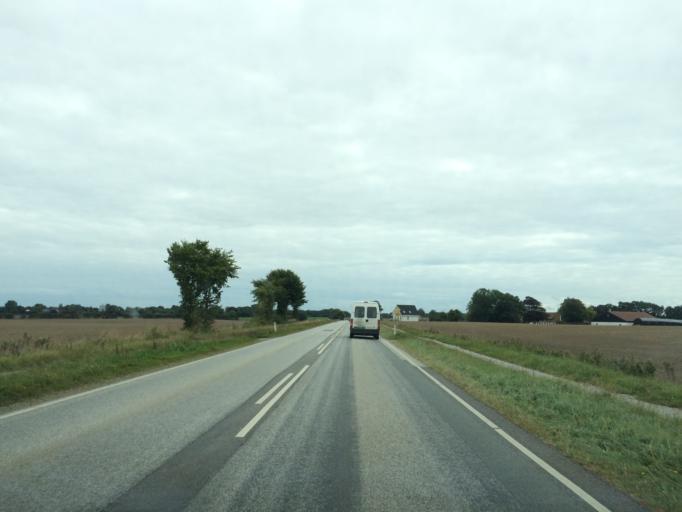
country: DK
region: South Denmark
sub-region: Sonderborg Kommune
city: Broager
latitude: 54.9657
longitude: 9.6735
